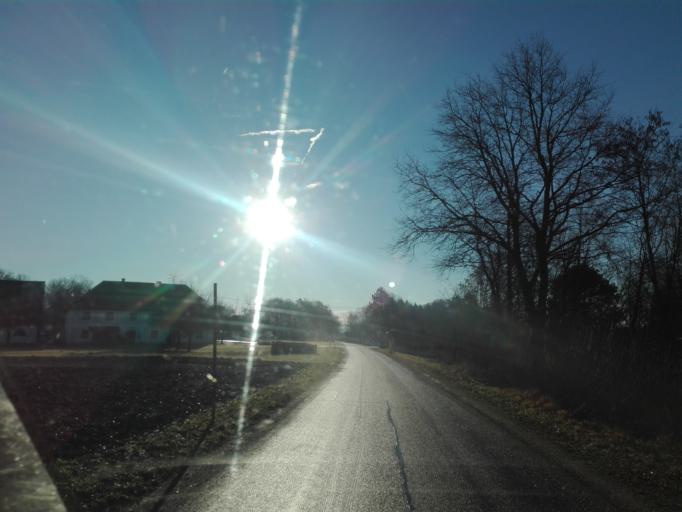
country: AT
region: Upper Austria
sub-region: Politischer Bezirk Perg
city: Perg
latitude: 48.2092
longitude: 14.6824
